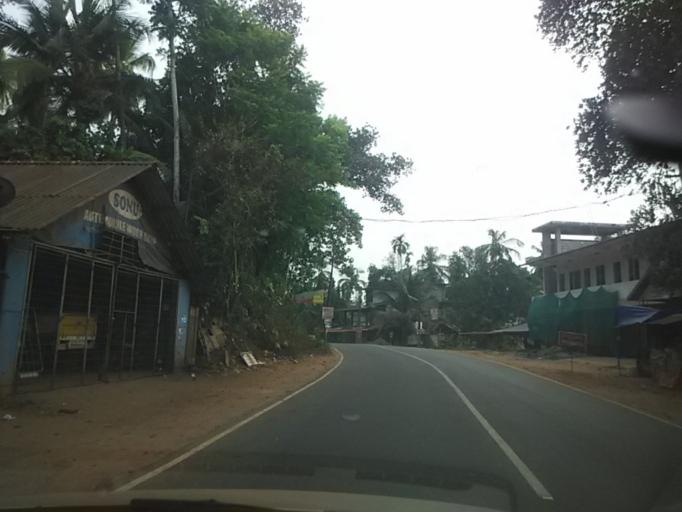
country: IN
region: Kerala
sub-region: Kozhikode
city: Naduvannur
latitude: 11.5413
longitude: 75.7693
